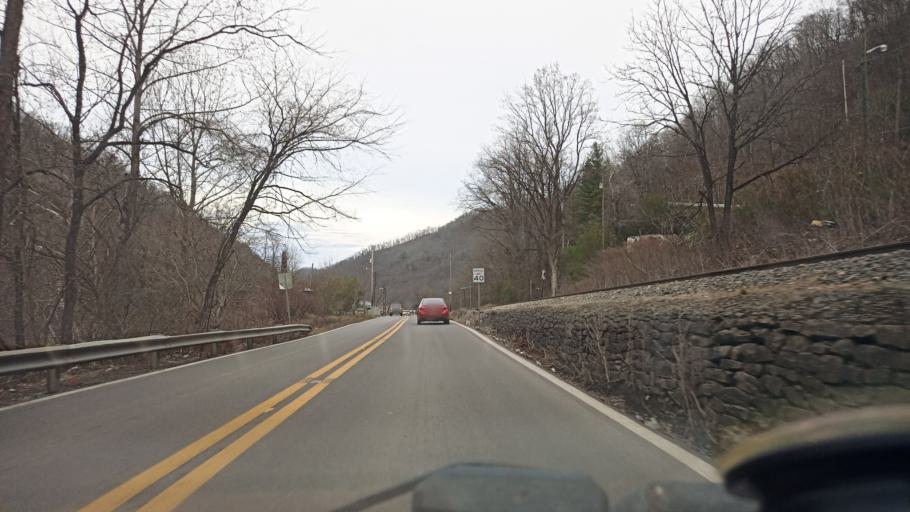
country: US
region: West Virginia
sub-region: Logan County
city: Mallory
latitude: 37.7079
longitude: -81.8668
